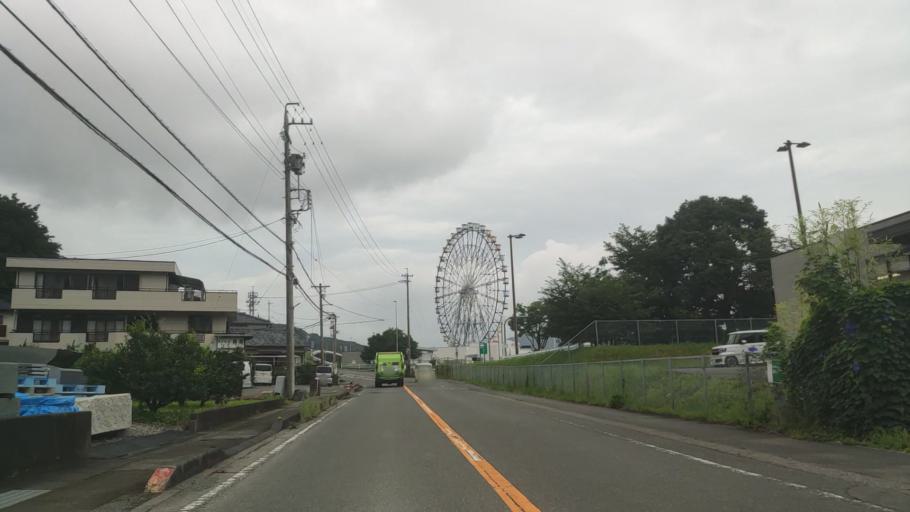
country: JP
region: Shizuoka
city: Fujinomiya
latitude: 35.1597
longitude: 138.6167
